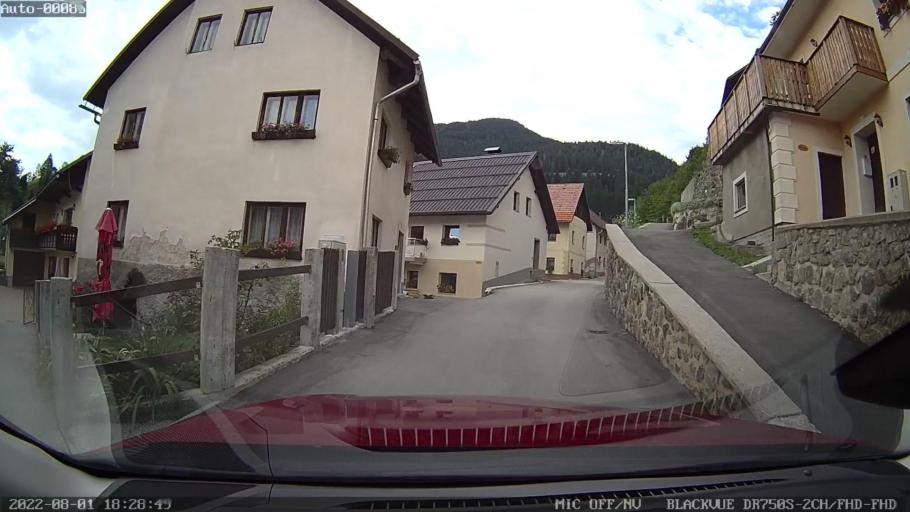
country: AT
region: Carinthia
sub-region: Politischer Bezirk Villach Land
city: Arnoldstein
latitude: 46.4985
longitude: 13.7161
